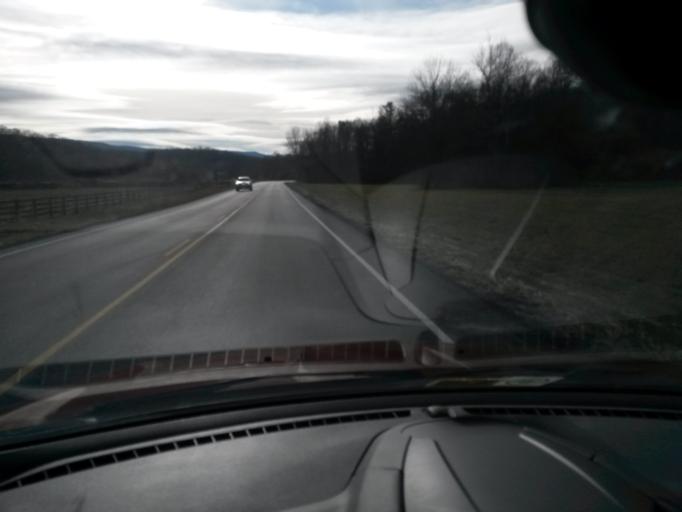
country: US
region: Virginia
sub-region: Augusta County
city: Jolivue
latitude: 38.1181
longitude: -79.2913
